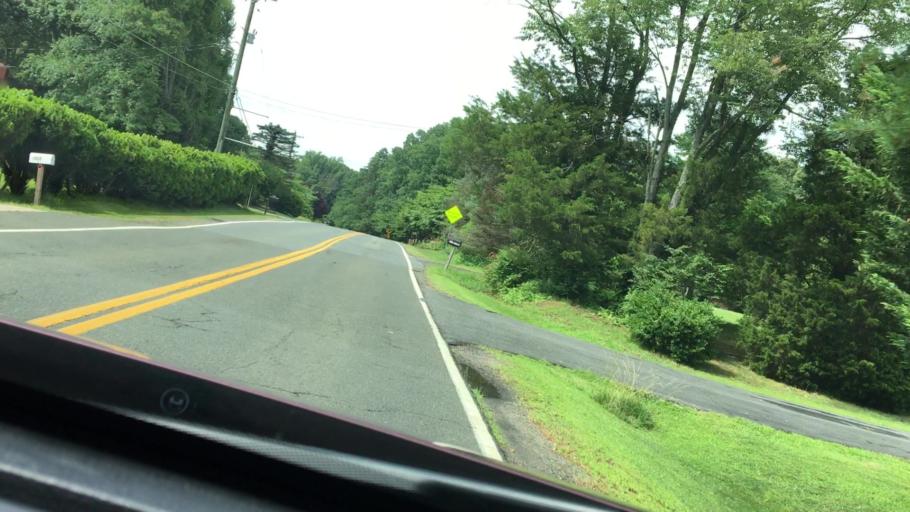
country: US
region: Virginia
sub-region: Prince William County
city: Buckhall
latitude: 38.7360
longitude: -77.4337
